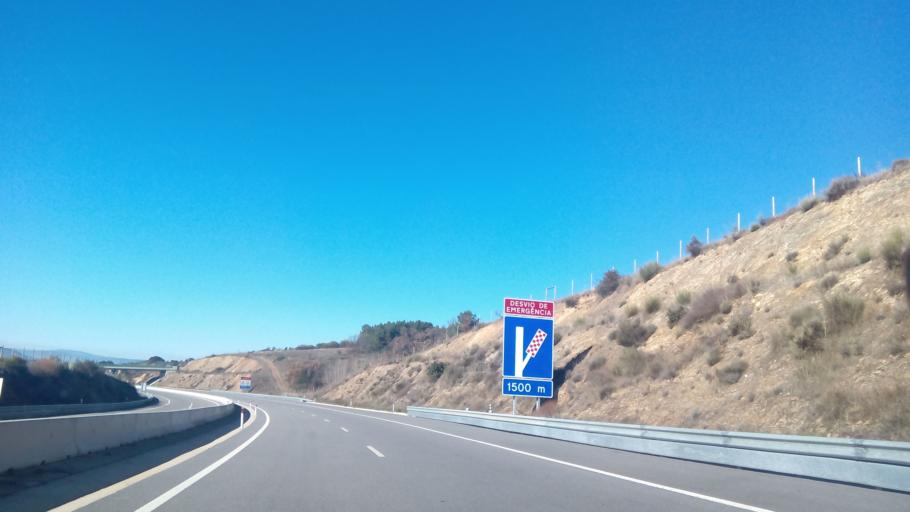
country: PT
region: Braganca
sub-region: Braganca Municipality
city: Braganca
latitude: 41.7523
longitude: -6.6310
